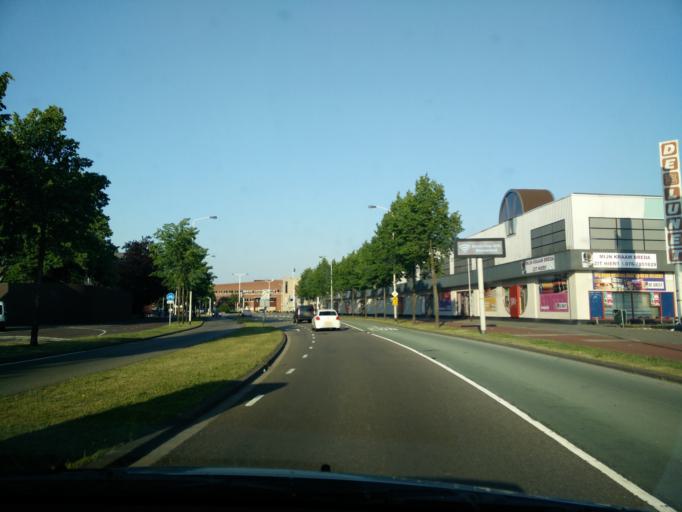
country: NL
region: North Brabant
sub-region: Gemeente Breda
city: Breda
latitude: 51.5892
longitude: 4.7612
